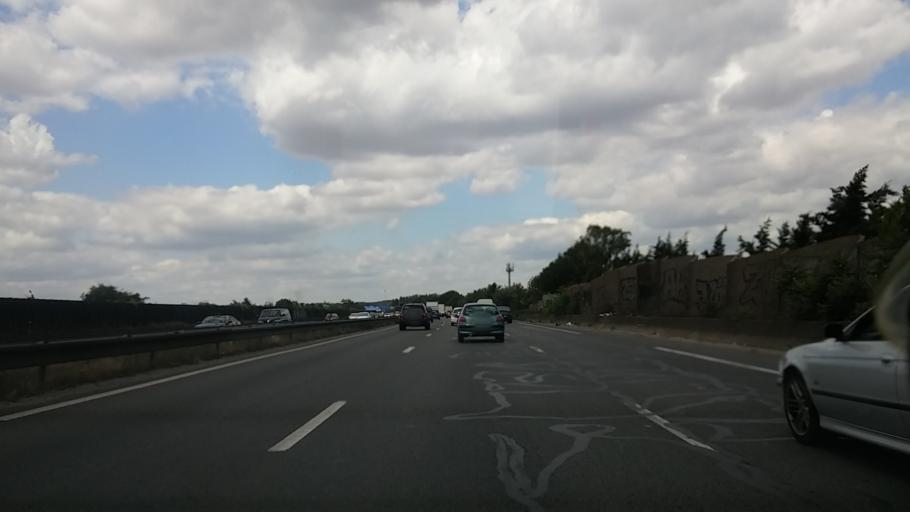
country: FR
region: Ile-de-France
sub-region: Departement de Seine-Saint-Denis
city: Aulnay-sous-Bois
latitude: 48.9361
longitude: 2.4805
